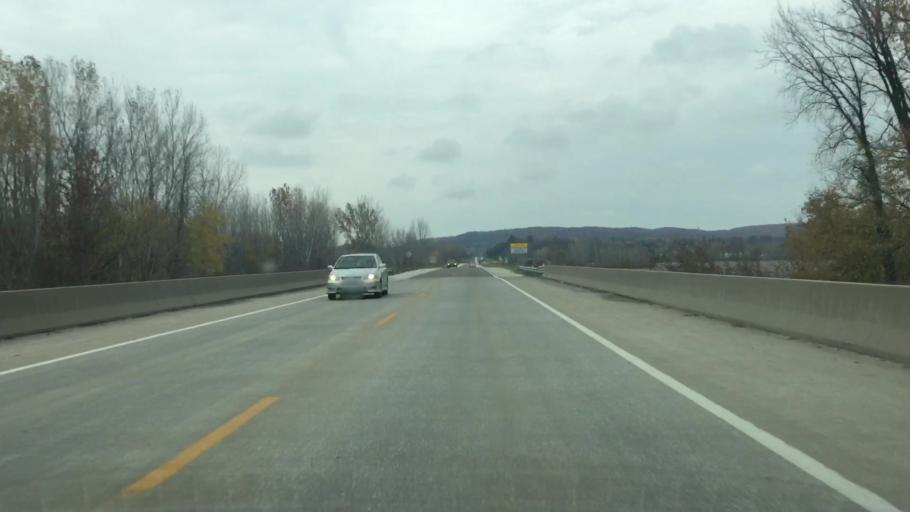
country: US
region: Missouri
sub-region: Gasconade County
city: Hermann
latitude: 38.7197
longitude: -91.4427
